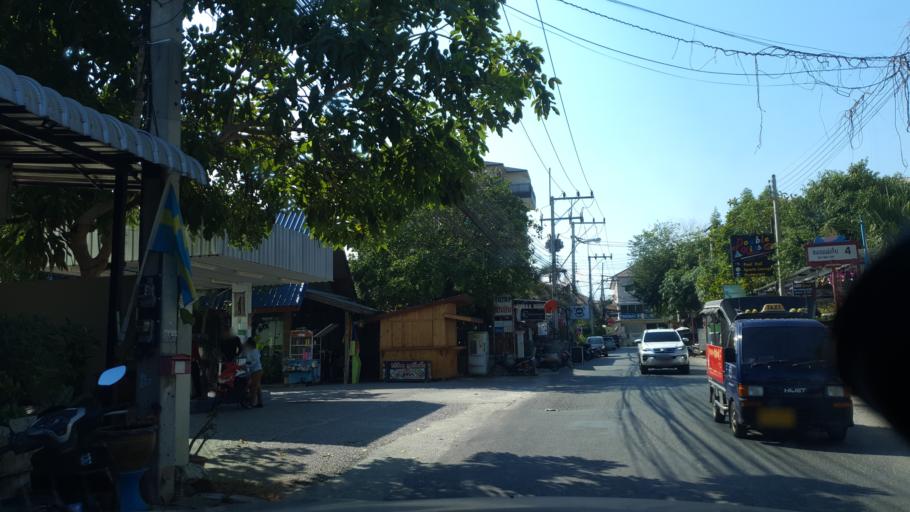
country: TH
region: Prachuap Khiri Khan
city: Hua Hin
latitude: 12.5547
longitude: 99.9536
